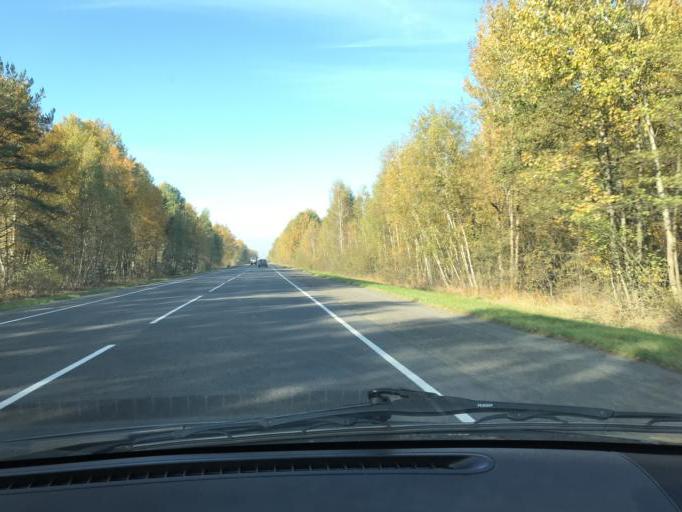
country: BY
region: Brest
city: Horad Luninyets
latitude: 52.2968
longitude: 26.7424
